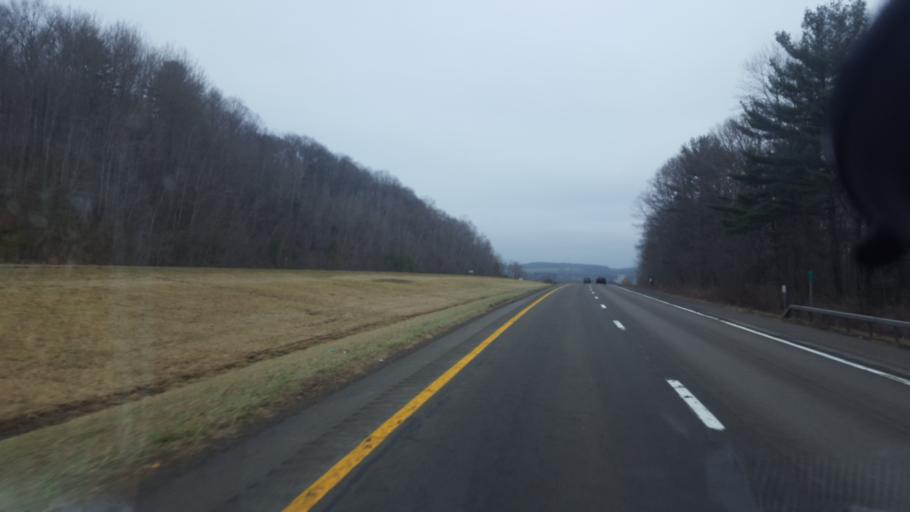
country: US
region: New York
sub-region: Chautauqua County
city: Falconer
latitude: 42.1380
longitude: -79.1201
